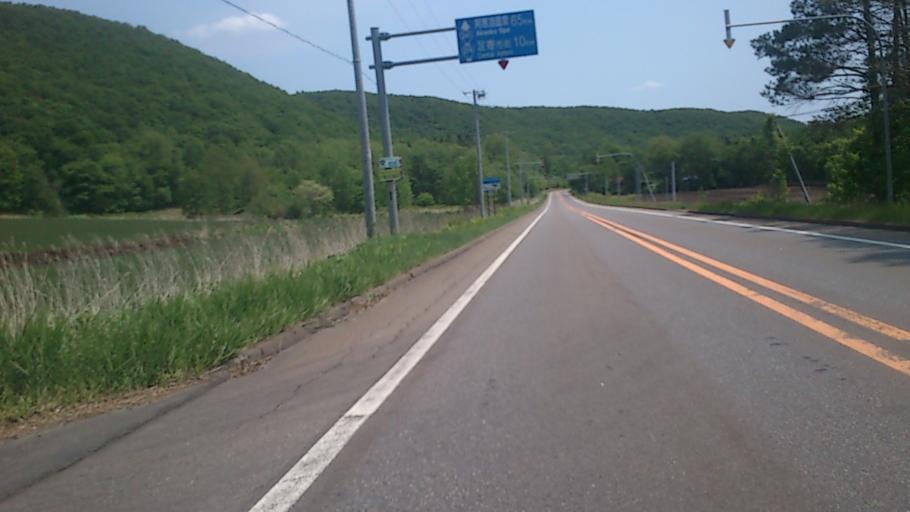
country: JP
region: Hokkaido
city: Otofuke
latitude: 43.2495
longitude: 143.4808
